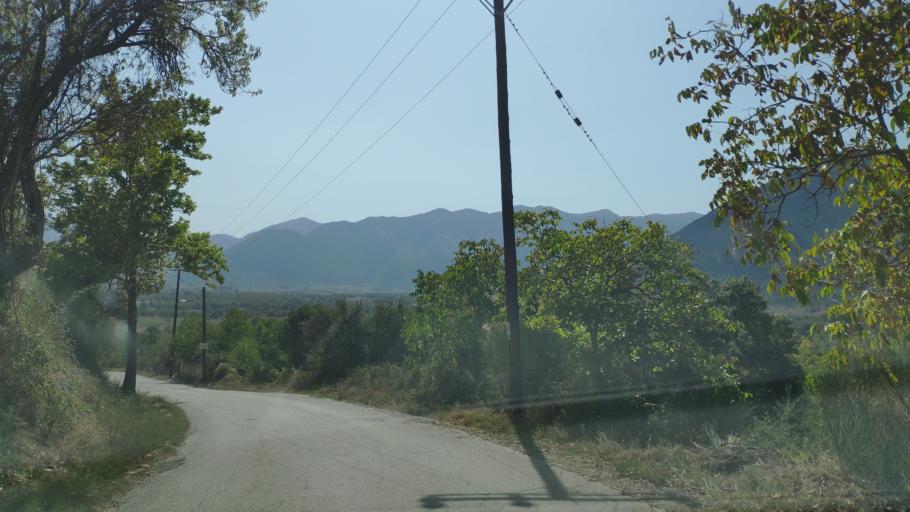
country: GR
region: West Greece
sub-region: Nomos Achaias
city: Kalavryta
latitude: 37.9159
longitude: 22.2990
